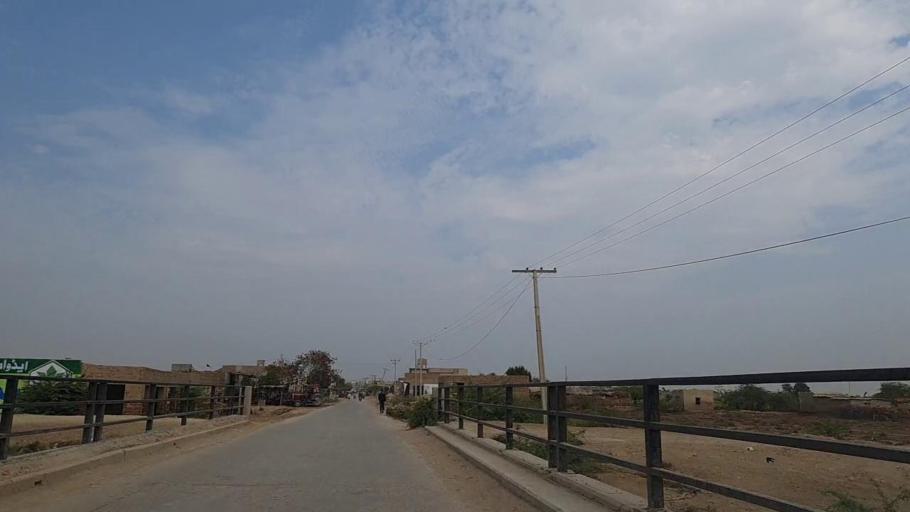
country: PK
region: Sindh
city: Naukot
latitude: 24.9586
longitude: 69.2875
